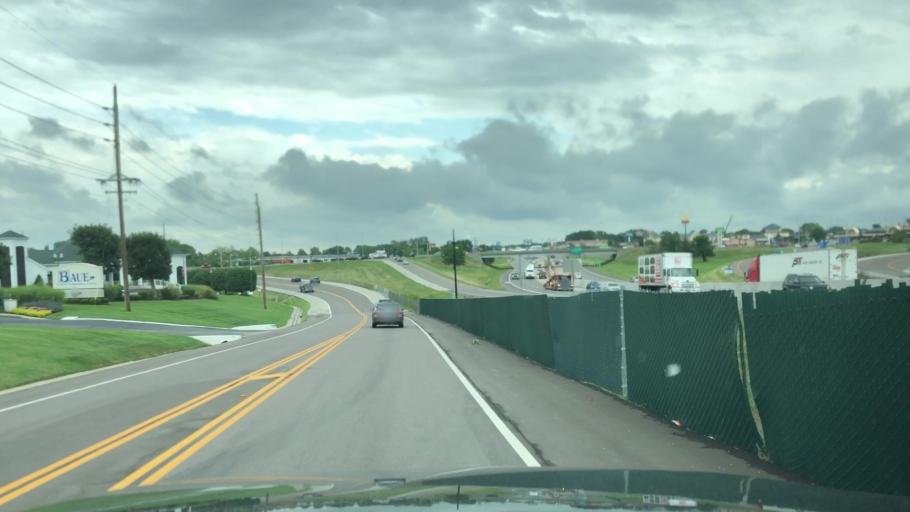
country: US
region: Missouri
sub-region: Saint Charles County
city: Saint Peters
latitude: 38.7954
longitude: -90.5689
